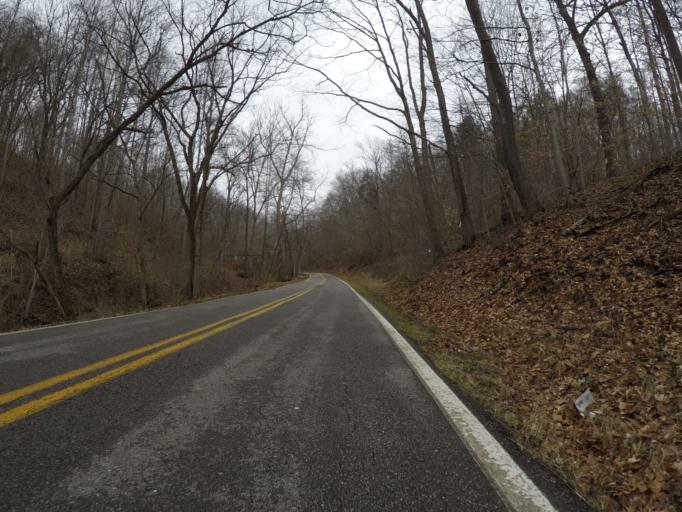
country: US
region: West Virginia
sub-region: Cabell County
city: Barboursville
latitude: 38.4529
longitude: -82.2626
